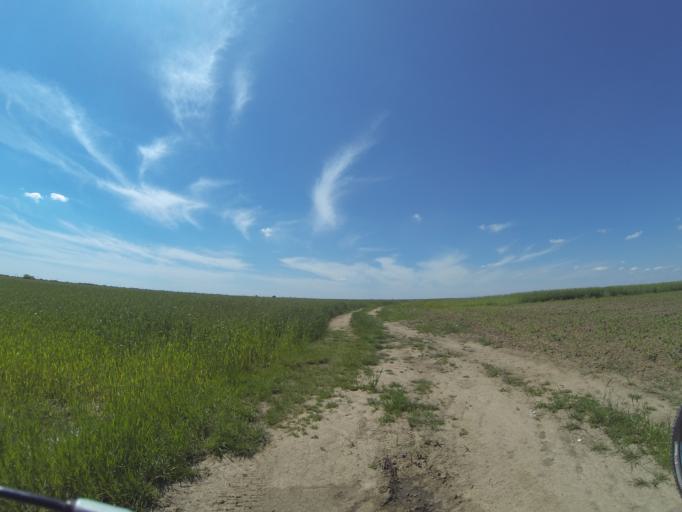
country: RO
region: Dolj
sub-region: Comuna Leu
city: Leu
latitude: 44.2209
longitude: 24.0074
